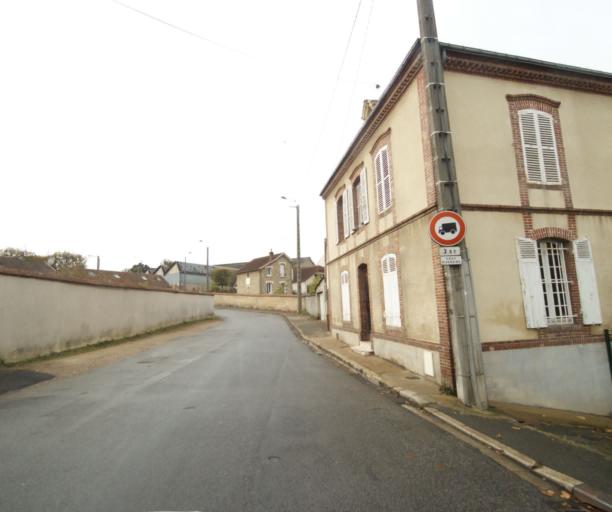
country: FR
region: Centre
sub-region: Departement d'Eure-et-Loir
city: Dreux
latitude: 48.7395
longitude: 1.3805
